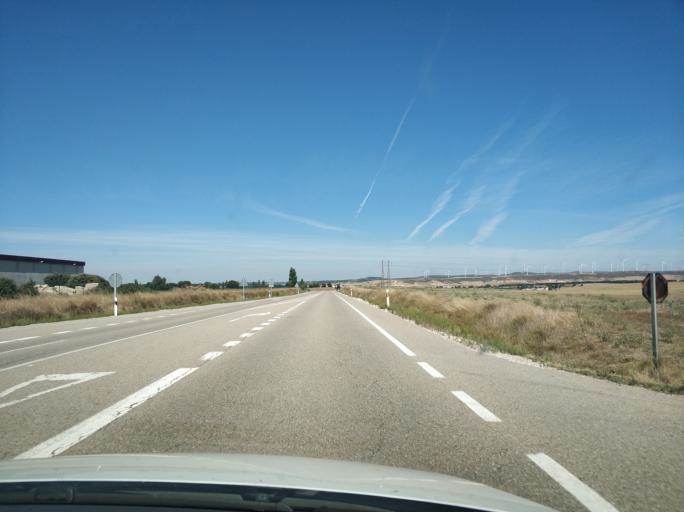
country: ES
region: Castille and Leon
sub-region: Provincia de Burgos
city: Hontoria de la Cantera
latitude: 42.2037
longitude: -3.6486
